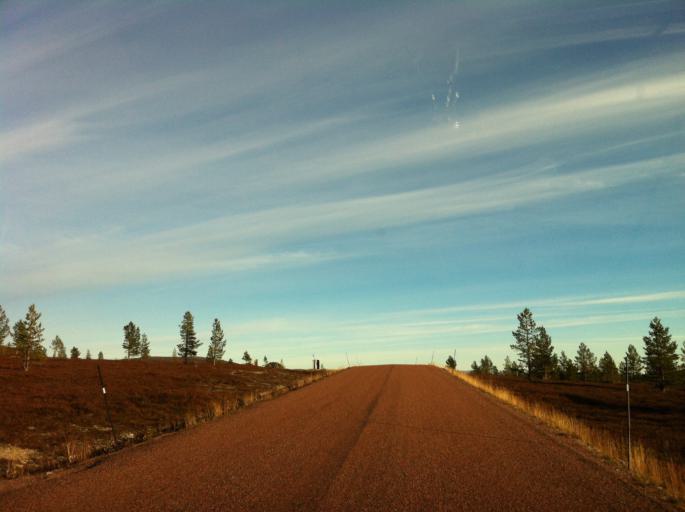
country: NO
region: Hedmark
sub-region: Engerdal
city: Engerdal
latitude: 62.0841
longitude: 12.0979
